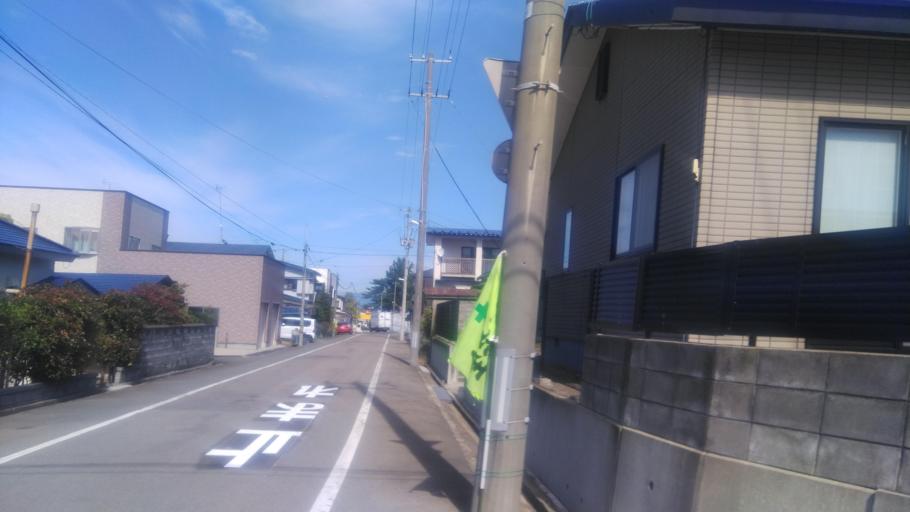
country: JP
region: Akita
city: Noshiromachi
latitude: 40.2037
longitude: 140.0279
